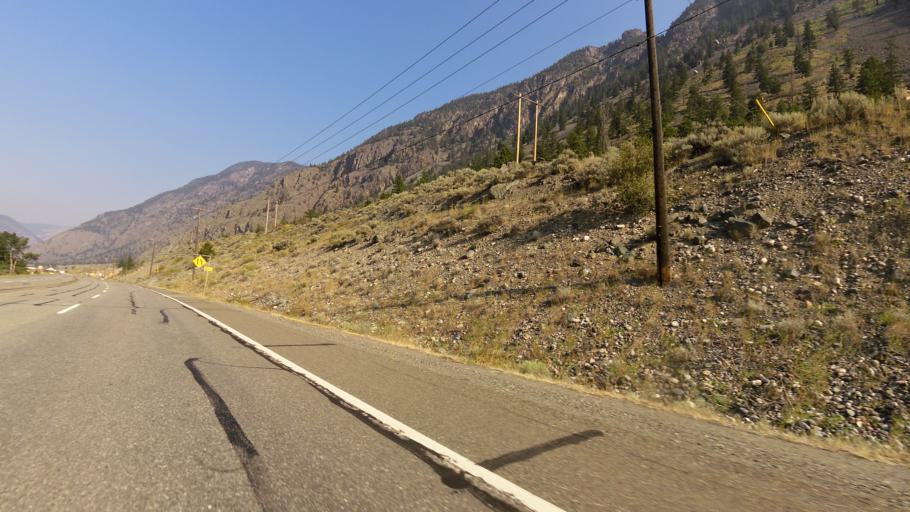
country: CA
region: British Columbia
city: Oliver
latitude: 49.2123
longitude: -119.8990
